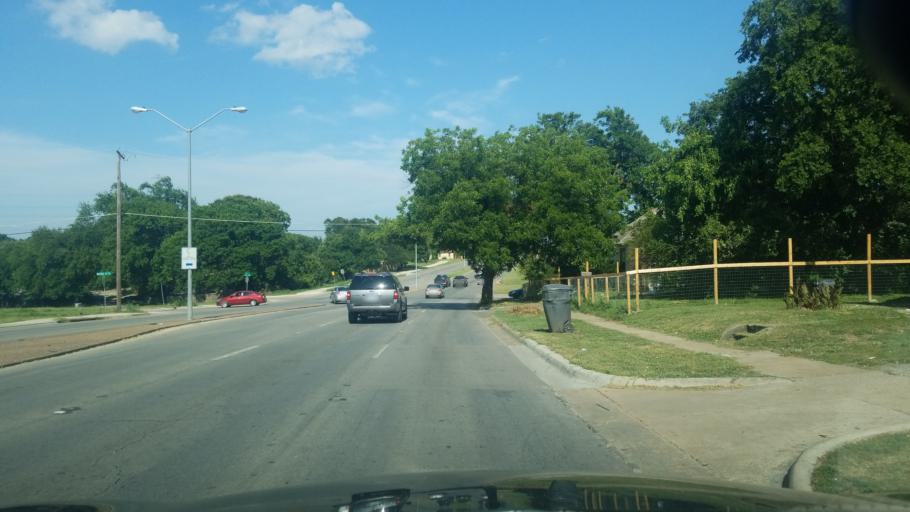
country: US
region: Texas
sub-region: Dallas County
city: Dallas
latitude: 32.7200
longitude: -96.8012
